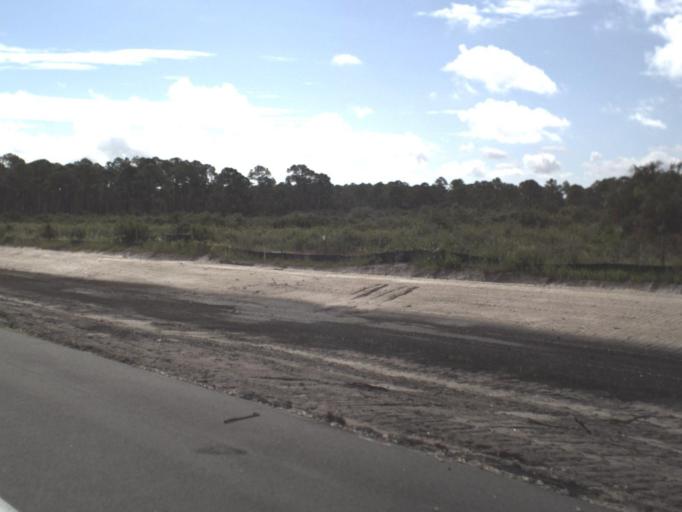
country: US
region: Florida
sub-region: Sarasota County
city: Warm Mineral Springs
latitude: 27.0998
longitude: -82.2699
